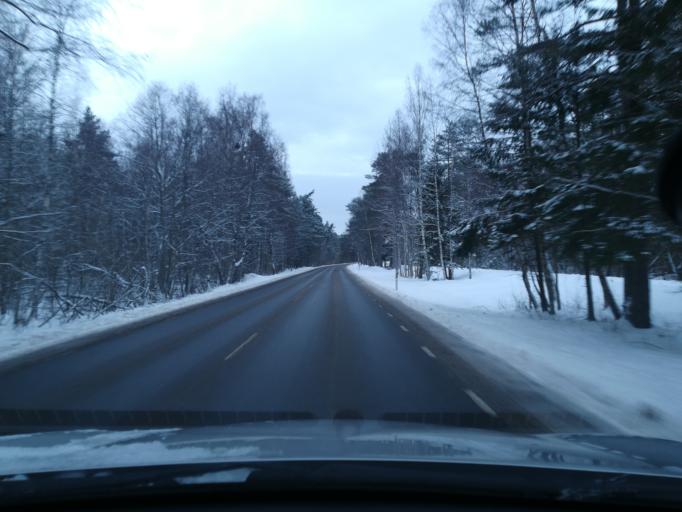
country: EE
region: Harju
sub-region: Paldiski linn
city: Paldiski
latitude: 59.3915
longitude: 24.2417
